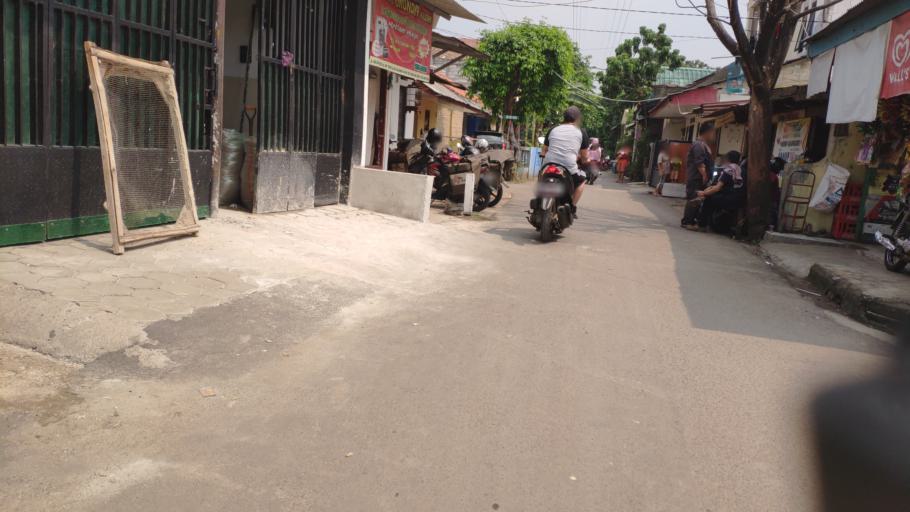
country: ID
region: West Java
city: Depok
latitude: -6.3240
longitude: 106.8276
